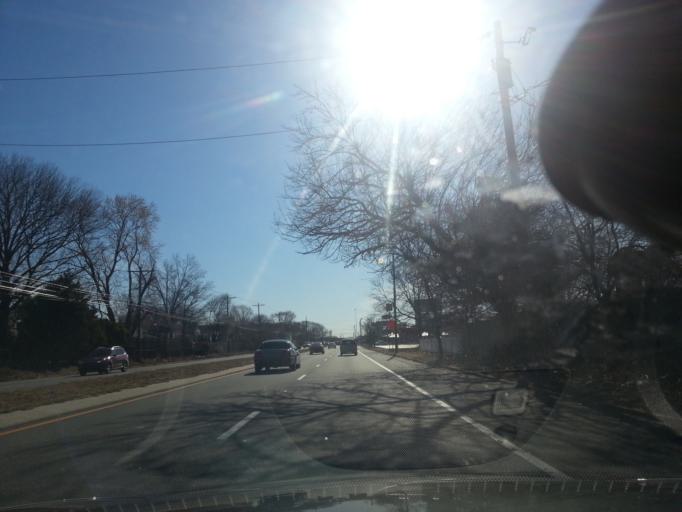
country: US
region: Delaware
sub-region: New Castle County
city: Brookside
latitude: 39.6768
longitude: -75.6853
